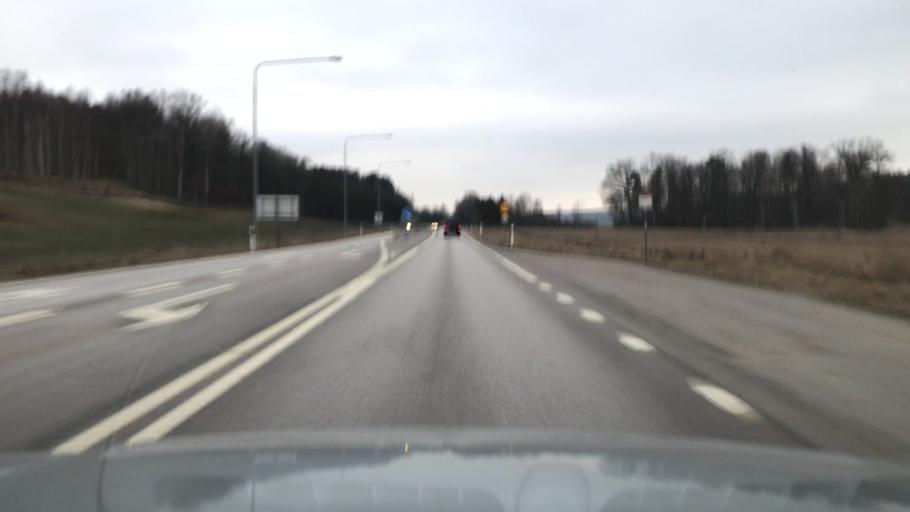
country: SE
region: OEstergoetland
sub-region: Valdemarsviks Kommun
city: Gusum
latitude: 58.3181
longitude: 16.4790
